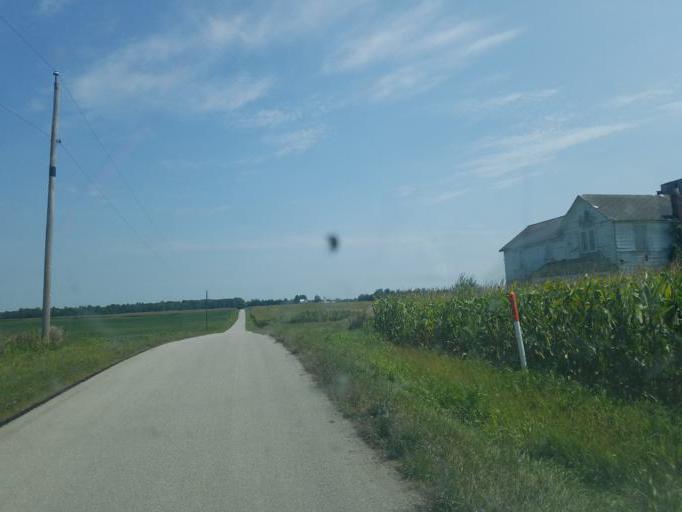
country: US
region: Ohio
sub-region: Crawford County
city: Bucyrus
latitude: 40.7532
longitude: -83.1199
